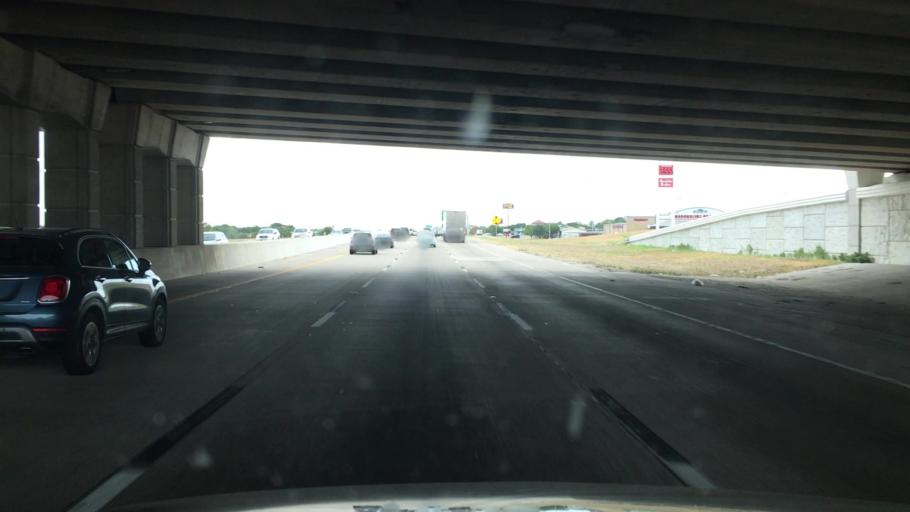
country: US
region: Texas
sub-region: McLennan County
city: Lorena
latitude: 31.3939
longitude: -97.2093
